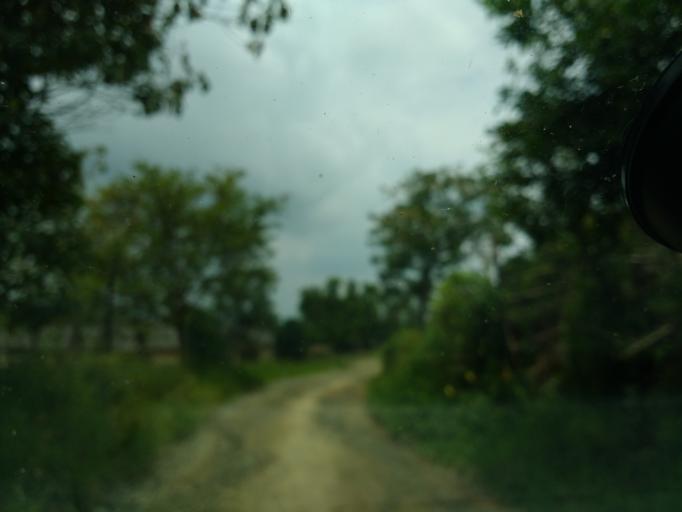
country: CO
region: Cauca
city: Santander de Quilichao
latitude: 2.9262
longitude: -76.4669
